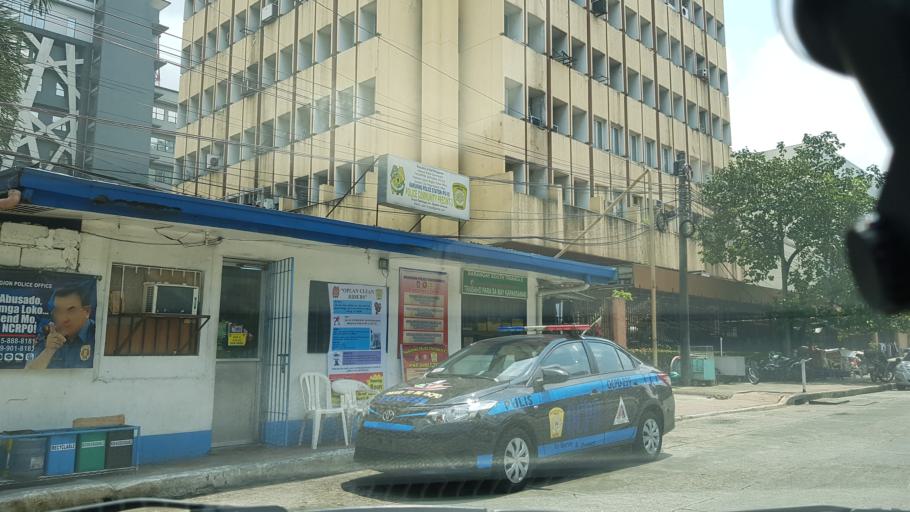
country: PH
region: Calabarzon
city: Del Monte
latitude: 14.6380
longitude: 121.0279
